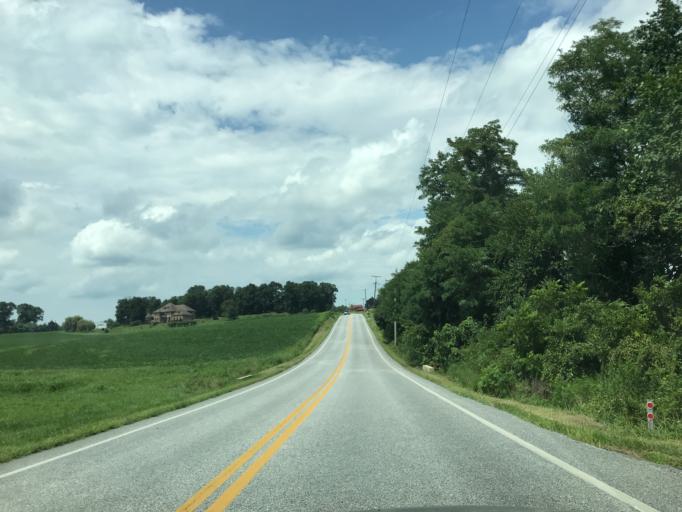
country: US
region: Pennsylvania
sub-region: York County
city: New Freedom
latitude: 39.7133
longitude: -76.7568
